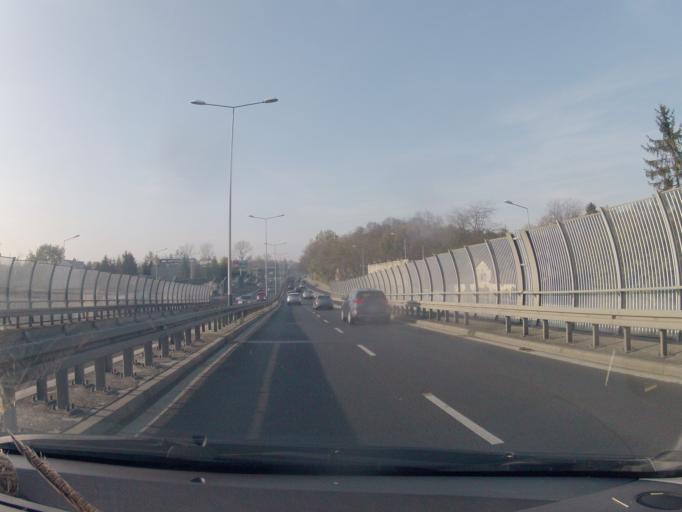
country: PL
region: Lesser Poland Voivodeship
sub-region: Powiat krakowski
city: Rzaska
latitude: 50.0886
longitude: 19.8872
